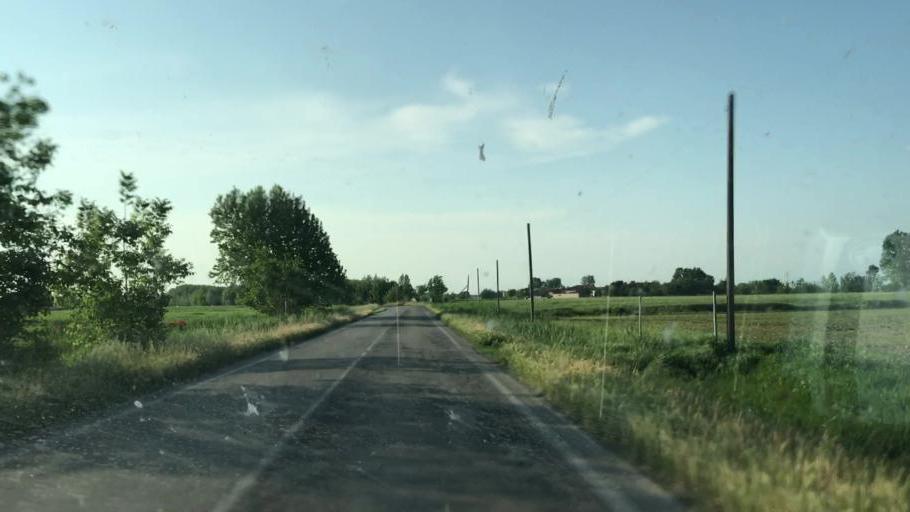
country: IT
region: Lombardy
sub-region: Provincia di Mantova
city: Piubega
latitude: 45.2404
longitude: 10.5074
